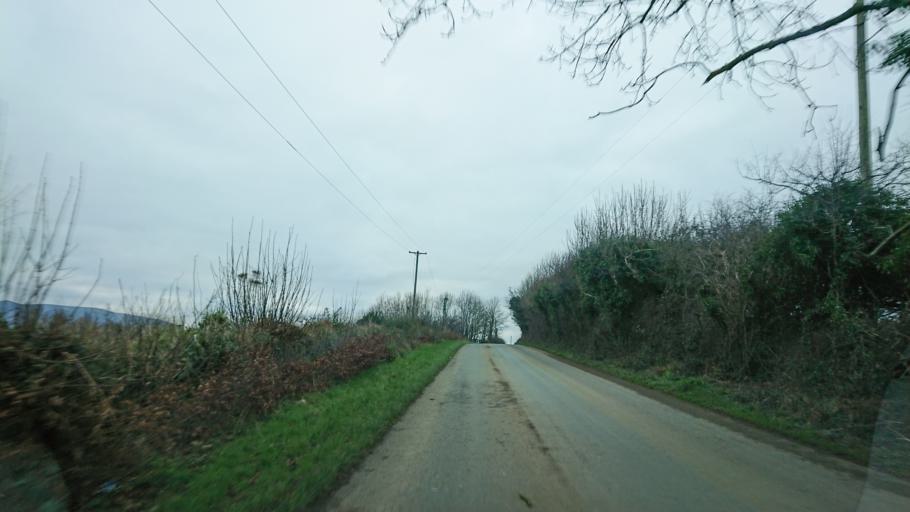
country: IE
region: Munster
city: Carrick-on-Suir
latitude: 52.2764
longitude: -7.4231
